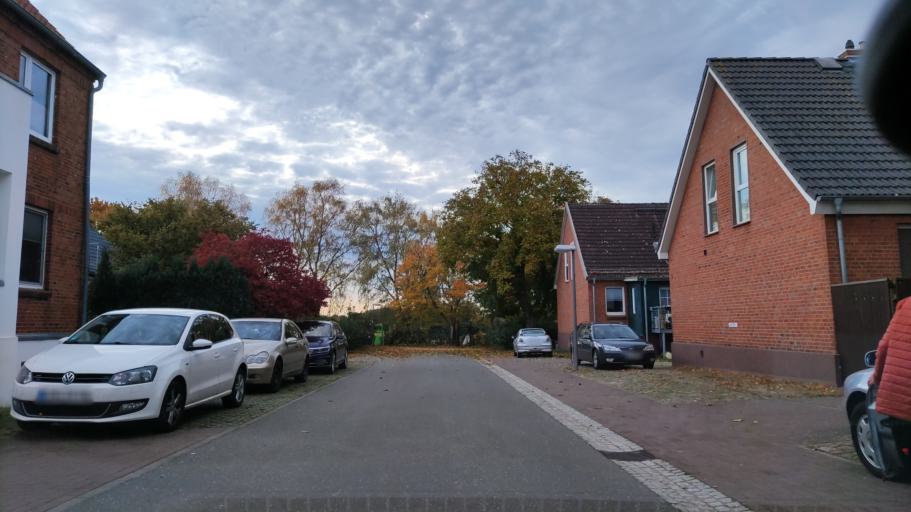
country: DE
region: Mecklenburg-Vorpommern
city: Boizenburg
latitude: 53.3750
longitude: 10.7472
